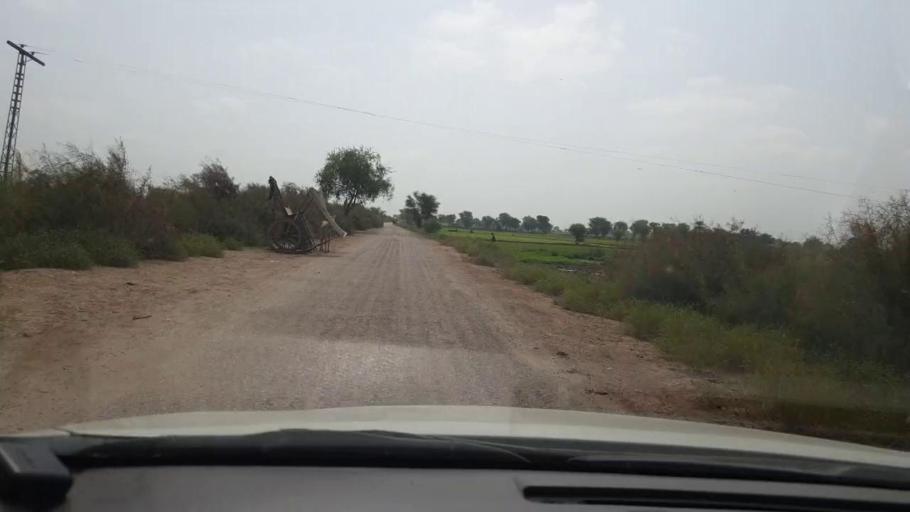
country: PK
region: Sindh
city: Shikarpur
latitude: 28.0076
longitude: 68.5766
